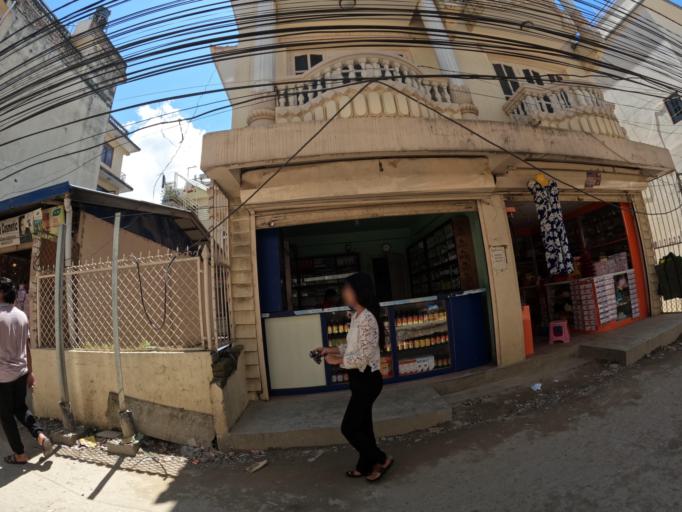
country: NP
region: Central Region
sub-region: Bagmati Zone
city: Kathmandu
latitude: 27.7388
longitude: 85.3243
